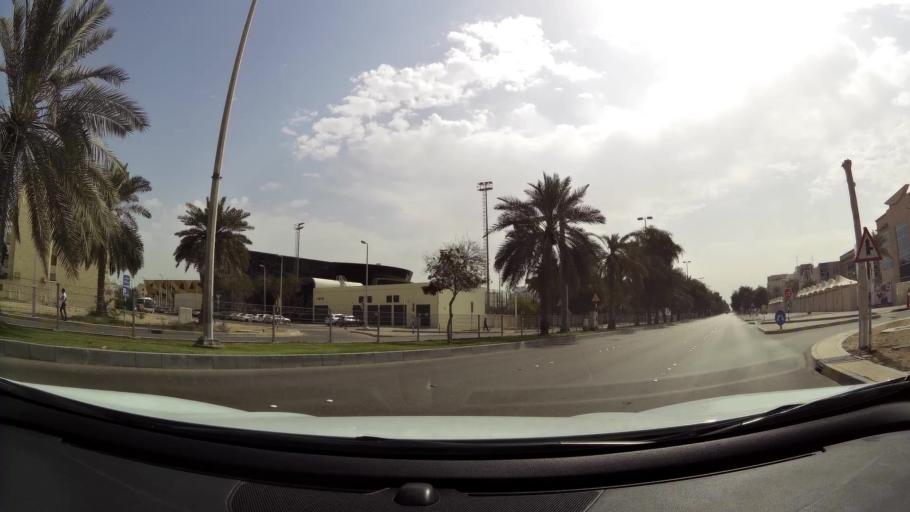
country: AE
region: Abu Dhabi
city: Abu Dhabi
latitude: 24.4577
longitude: 54.3596
